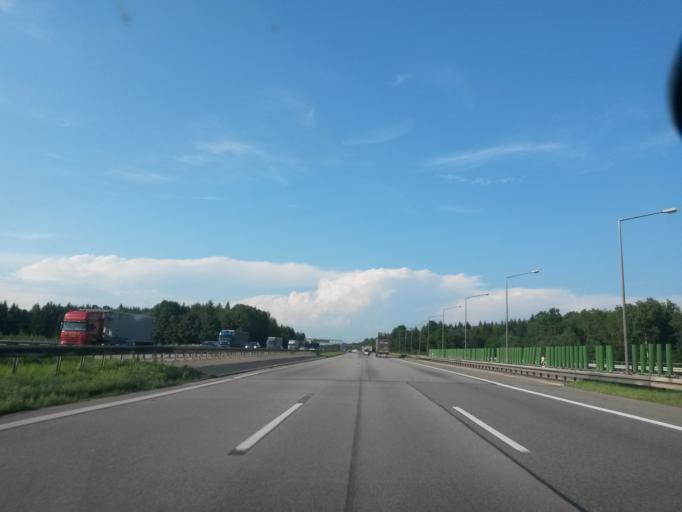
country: DE
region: Bavaria
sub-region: Upper Bavaria
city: Grasbrunn
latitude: 48.0891
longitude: 11.7441
